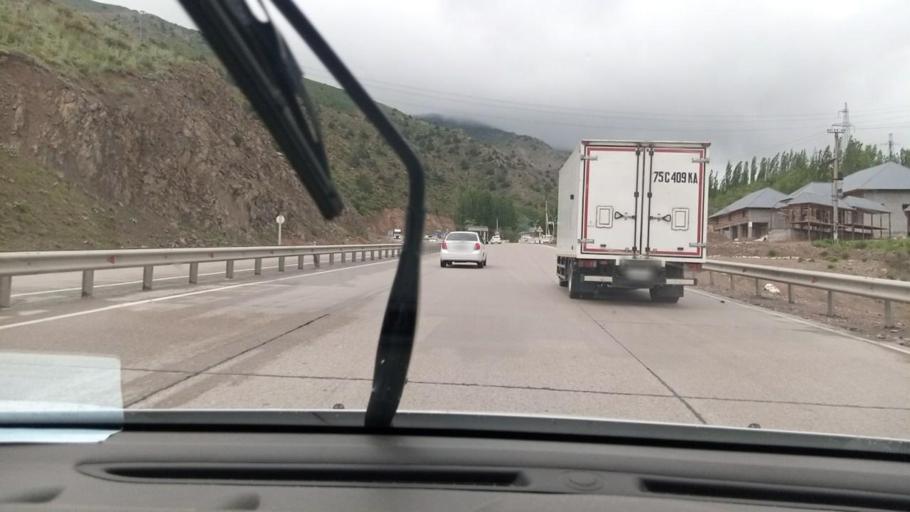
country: TJ
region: Viloyati Sughd
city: Shaydon
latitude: 41.0332
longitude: 70.5885
